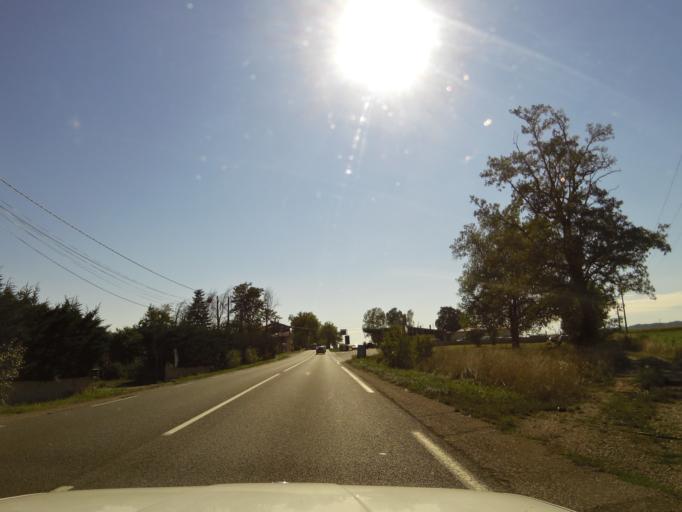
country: FR
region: Rhone-Alpes
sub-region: Departement de l'Ain
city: Leyment
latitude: 45.9226
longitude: 5.2711
